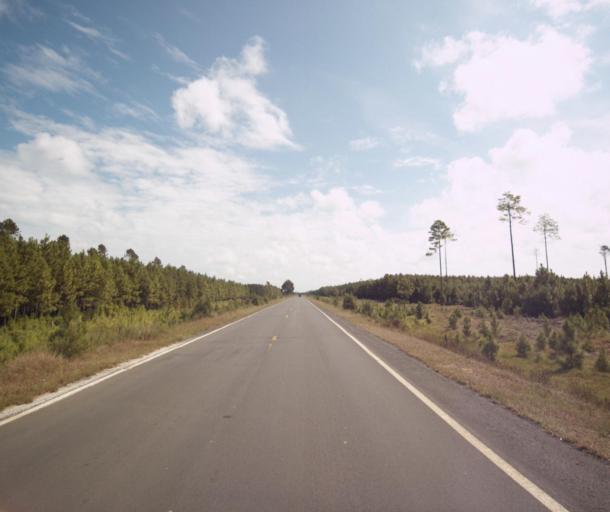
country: BR
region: Rio Grande do Sul
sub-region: Sao Lourenco Do Sul
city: Sao Lourenco do Sul
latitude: -31.4477
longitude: -51.2083
